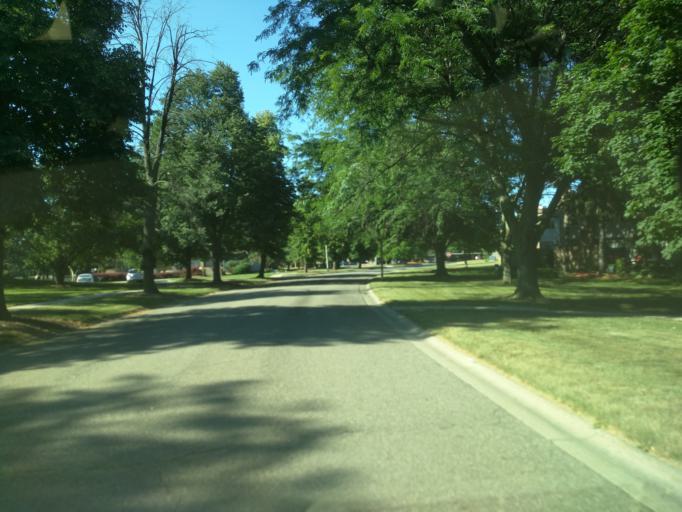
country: US
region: Michigan
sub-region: Eaton County
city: Waverly
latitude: 42.7241
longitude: -84.6349
